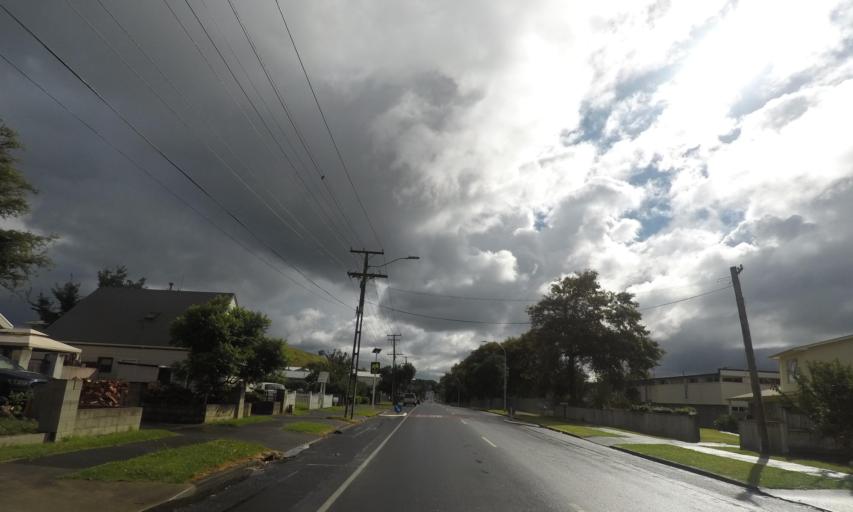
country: NZ
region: Auckland
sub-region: Auckland
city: Mangere
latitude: -36.9574
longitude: 174.7841
